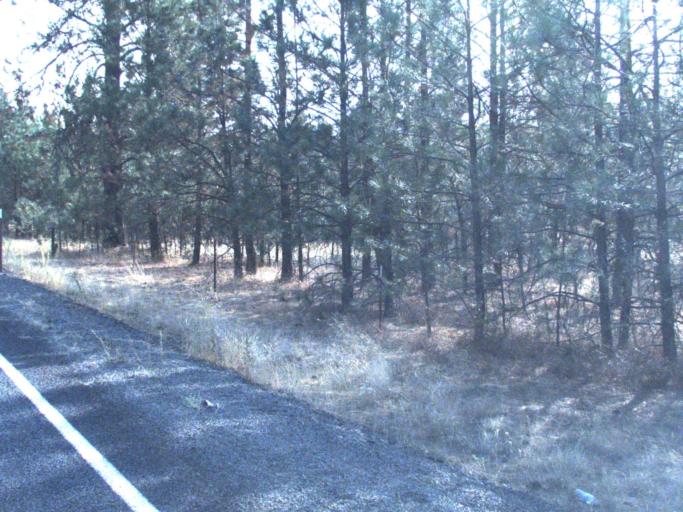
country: US
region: Washington
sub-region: Spokane County
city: Fairchild Air Force Base
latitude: 47.8396
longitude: -117.7471
